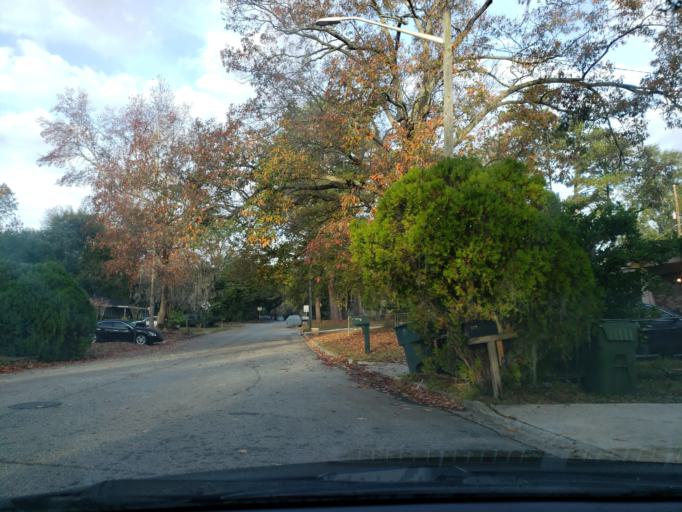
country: US
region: Georgia
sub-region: Chatham County
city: Montgomery
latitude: 31.9959
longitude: -81.1186
